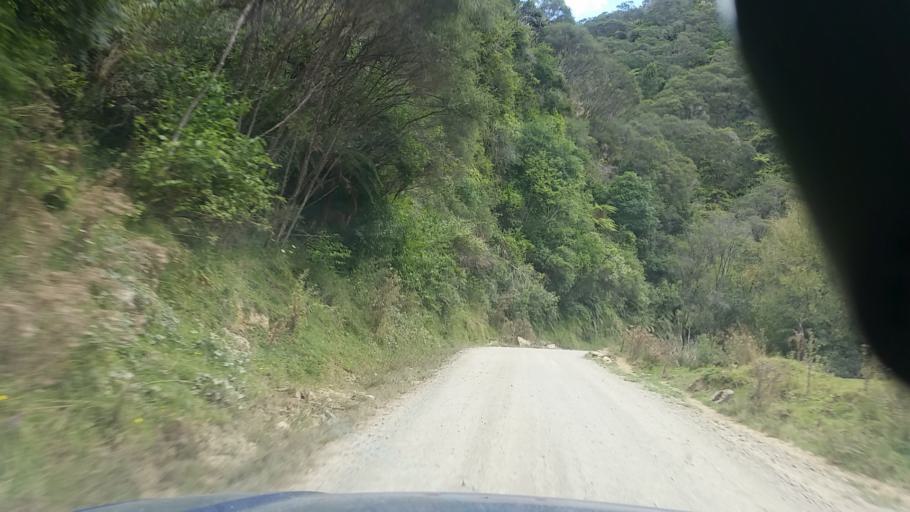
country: NZ
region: Taranaki
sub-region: New Plymouth District
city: Waitara
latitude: -39.0214
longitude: 174.8365
